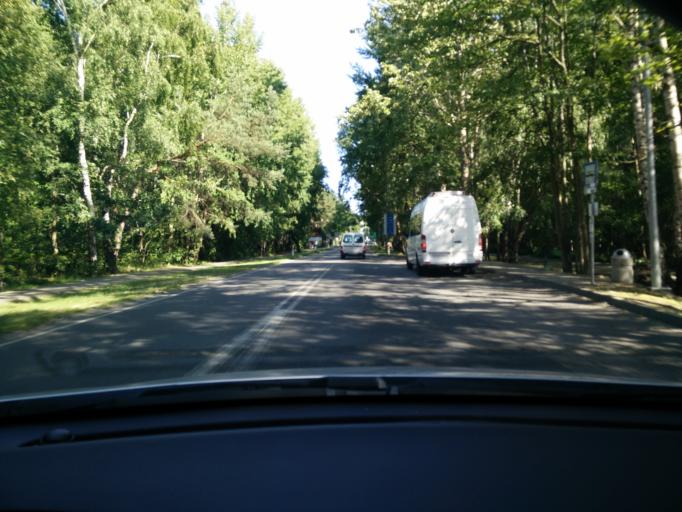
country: PL
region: Pomeranian Voivodeship
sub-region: Powiat pucki
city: Jastarnia
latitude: 54.7077
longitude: 18.6541
